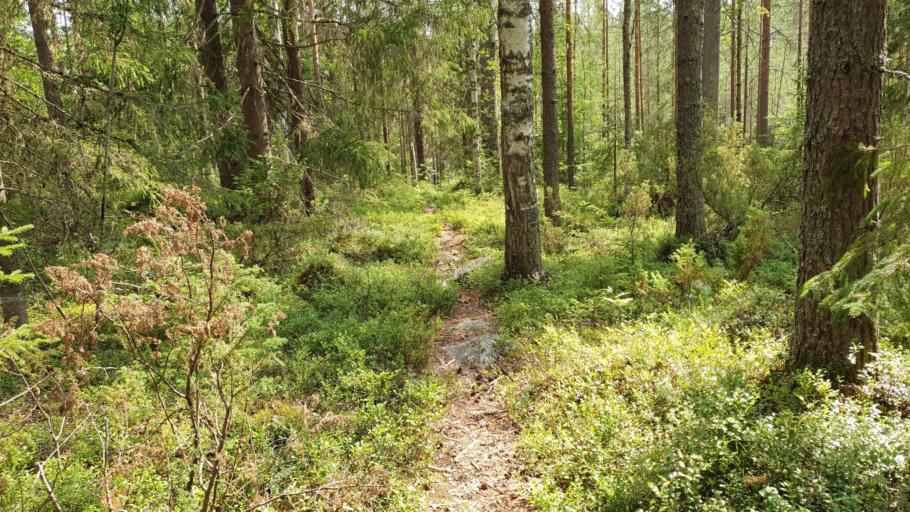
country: FI
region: Kainuu
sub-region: Kehys-Kainuu
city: Kuhmo
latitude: 64.2982
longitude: 29.2619
